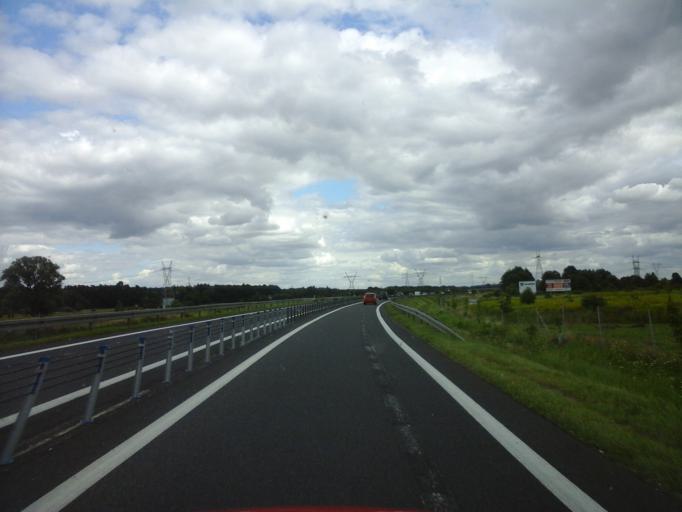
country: PL
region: West Pomeranian Voivodeship
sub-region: Powiat stargardzki
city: Kobylanka
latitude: 53.3594
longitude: 14.8810
